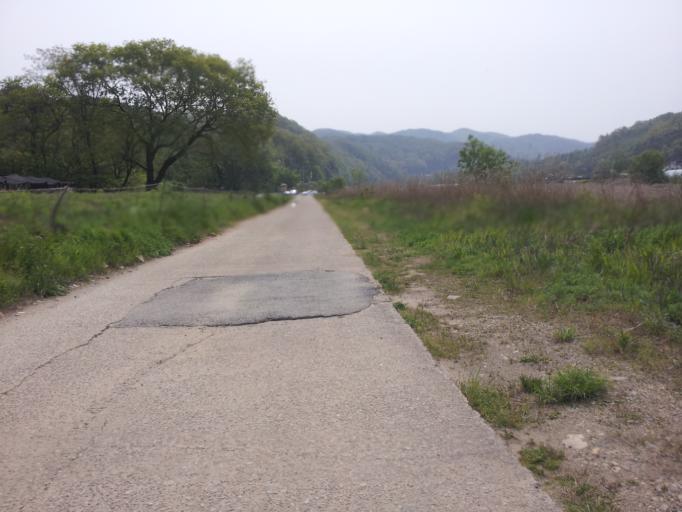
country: KR
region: Daejeon
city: Daejeon
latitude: 36.2721
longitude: 127.3386
